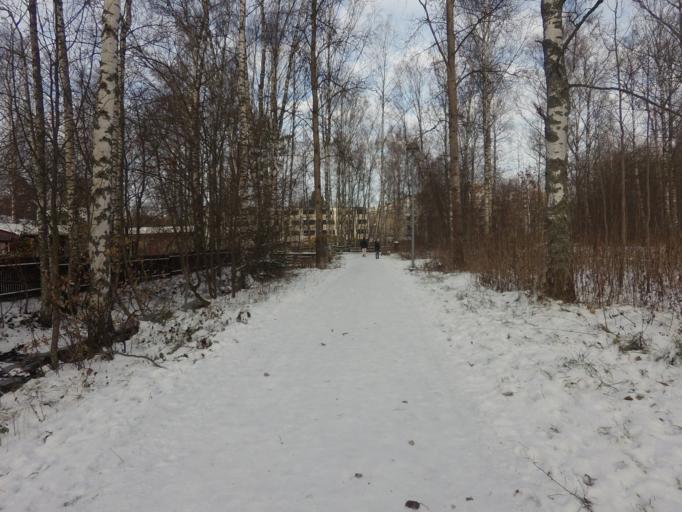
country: FI
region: Uusimaa
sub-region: Helsinki
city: Koukkuniemi
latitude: 60.1504
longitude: 24.7426
